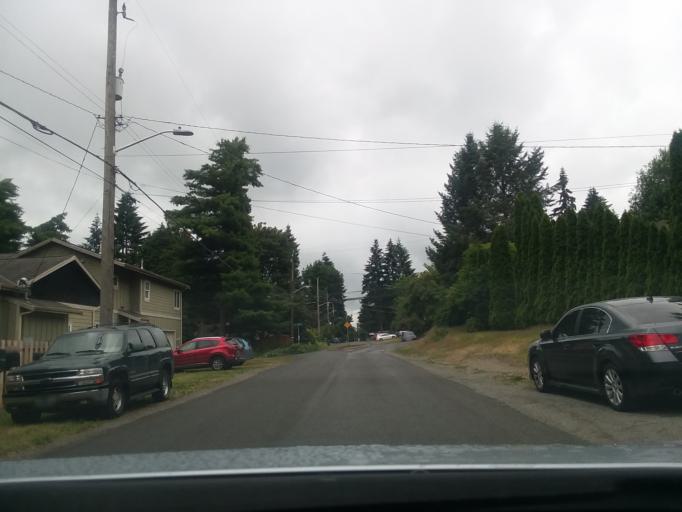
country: US
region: Washington
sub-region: King County
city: Lake Forest Park
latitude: 47.7162
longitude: -122.3018
